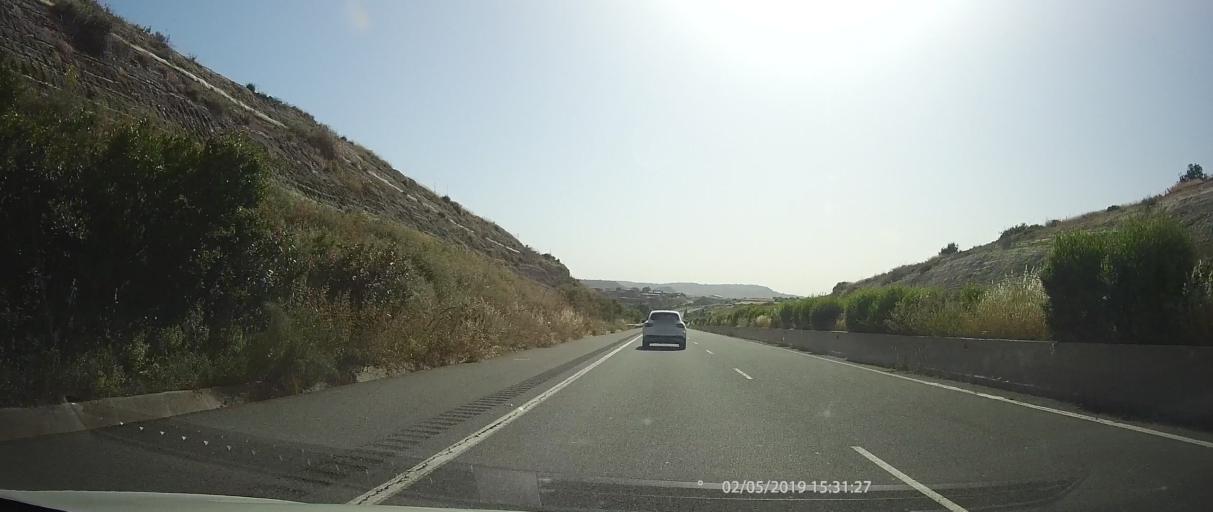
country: CY
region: Limassol
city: Pissouri
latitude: 34.6848
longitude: 32.7780
